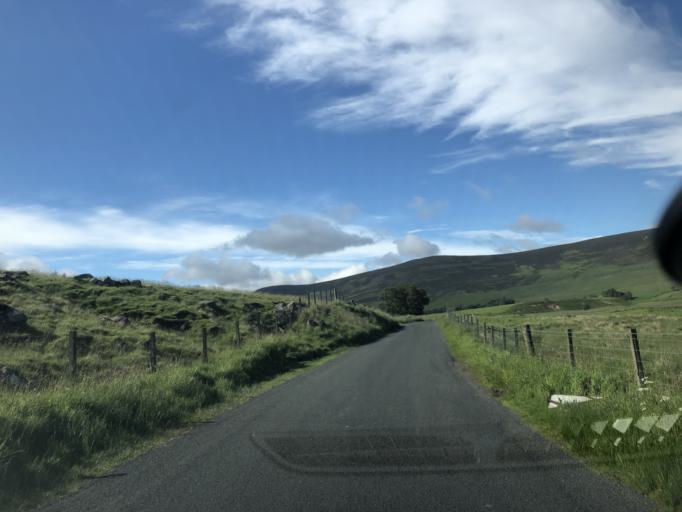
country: GB
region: Scotland
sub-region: Angus
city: Kirriemuir
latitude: 56.8057
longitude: -3.0355
